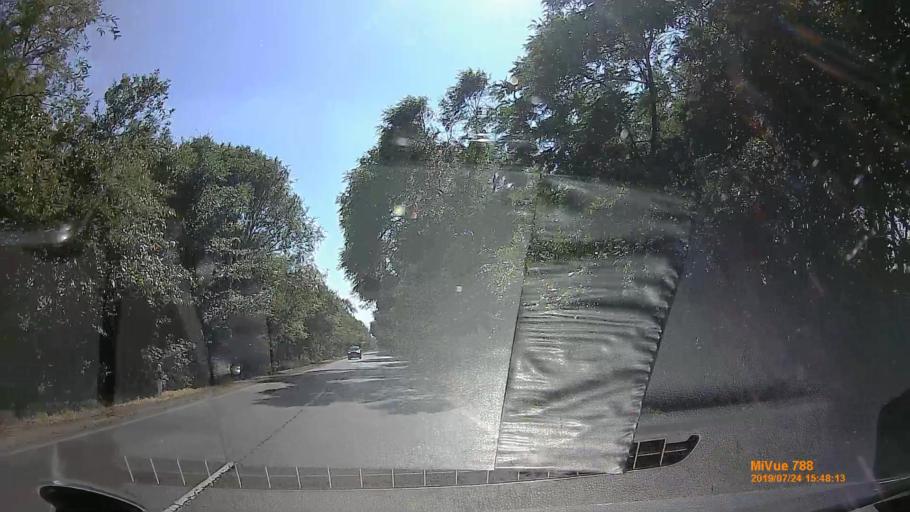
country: HU
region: Szabolcs-Szatmar-Bereg
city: Nyirmada
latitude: 48.0703
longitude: 22.2348
